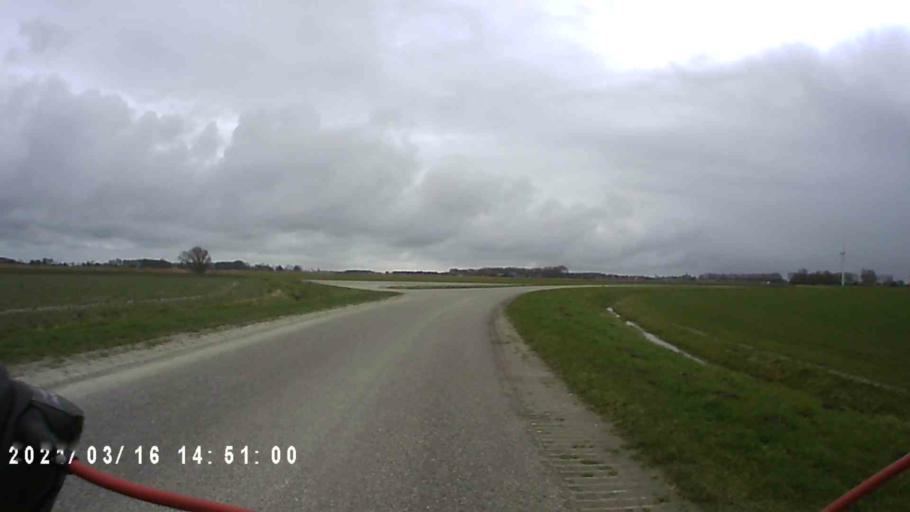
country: NL
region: Friesland
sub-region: Gemeente Harlingen
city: Harlingen
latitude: 53.1177
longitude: 5.4657
